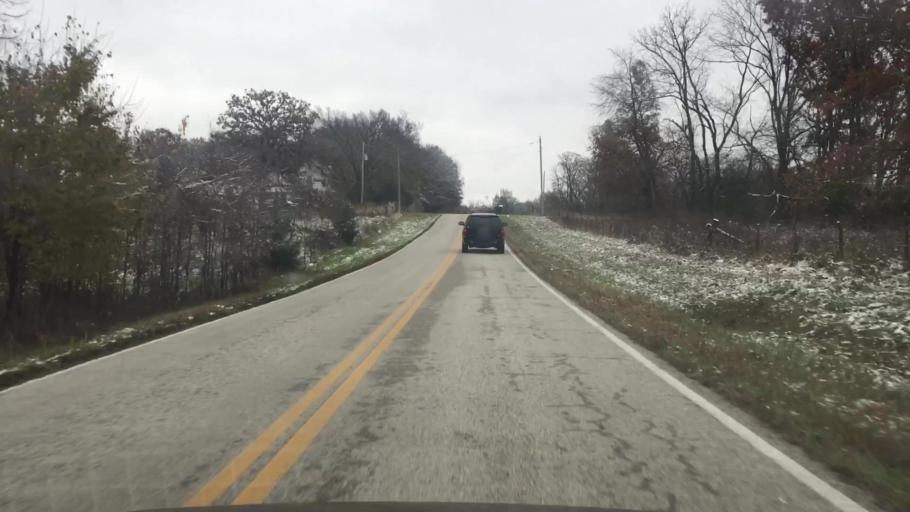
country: US
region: Missouri
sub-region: Saint Clair County
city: Osceola
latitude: 37.9890
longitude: -93.6164
